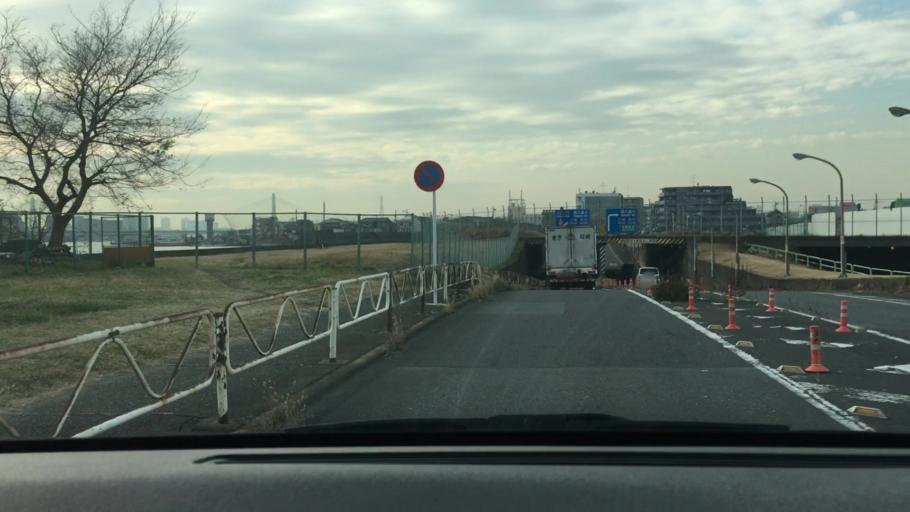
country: JP
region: Kanagawa
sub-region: Kawasaki-shi
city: Kawasaki
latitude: 35.5462
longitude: 139.7551
